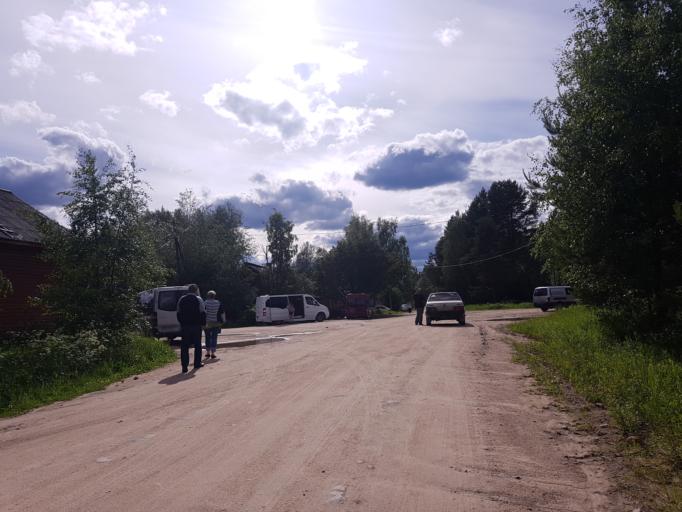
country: RU
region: Republic of Karelia
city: Kostomuksha
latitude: 64.9529
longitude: 30.5560
